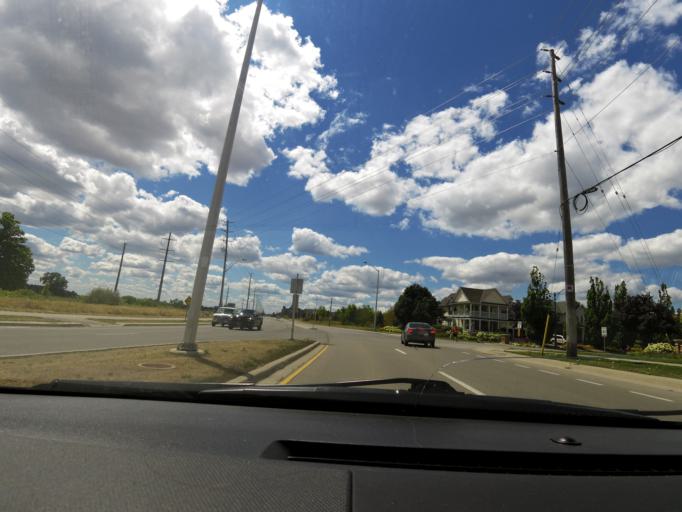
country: CA
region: Ontario
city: Burlington
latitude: 43.4071
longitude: -79.7762
